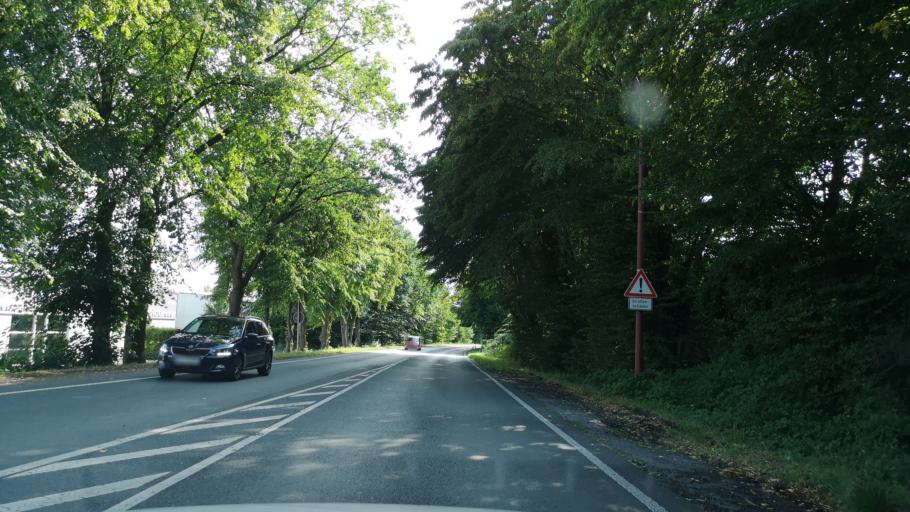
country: DE
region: North Rhine-Westphalia
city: Schwerte
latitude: 51.4569
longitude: 7.6124
